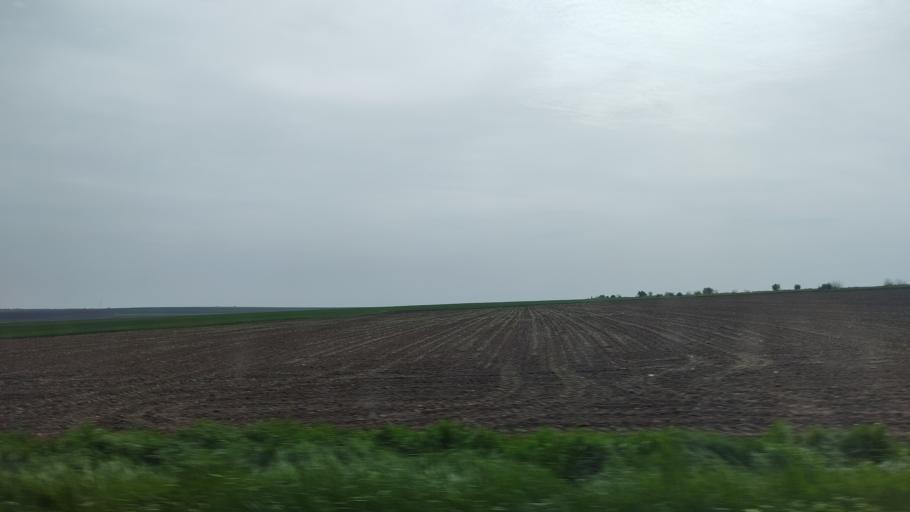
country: RO
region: Constanta
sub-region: Comuna Ciocarlia
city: Ciocarlia de Sus
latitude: 44.1347
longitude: 28.3479
